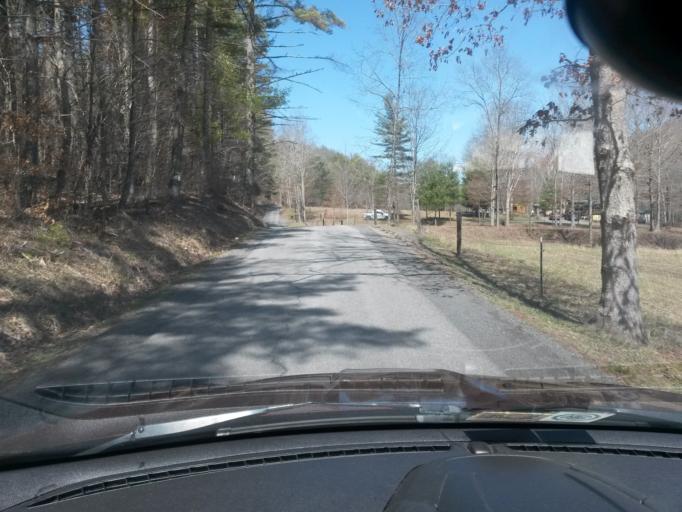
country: US
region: West Virginia
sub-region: Greenbrier County
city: White Sulphur Springs
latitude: 37.6497
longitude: -80.3273
